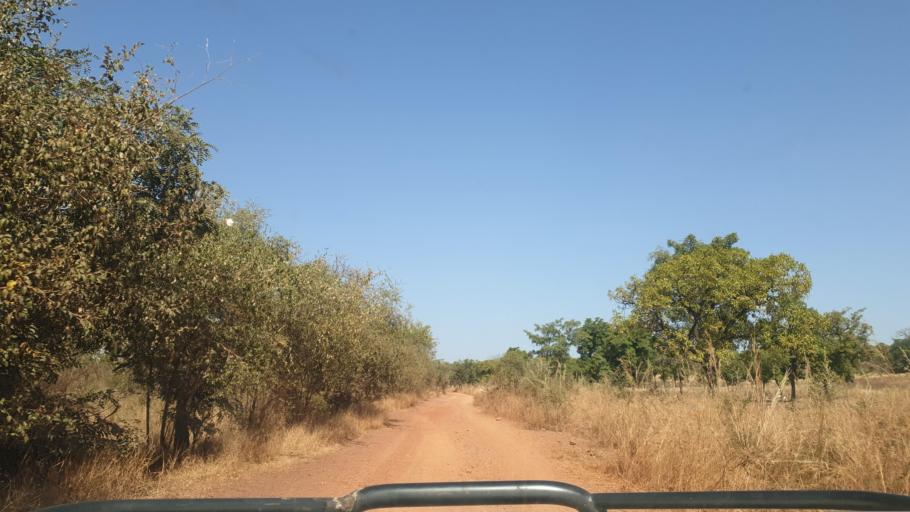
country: ML
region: Koulikoro
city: Dioila
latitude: 11.9078
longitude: -6.9835
